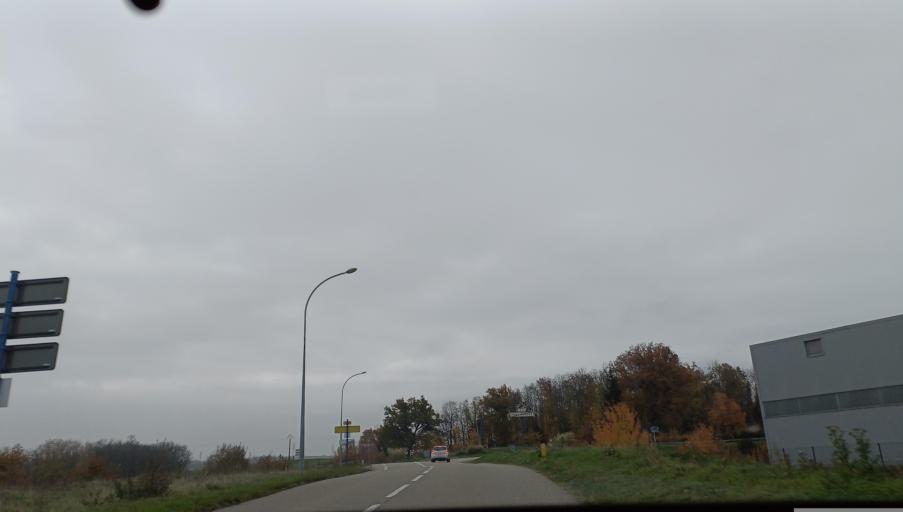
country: FR
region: Rhone-Alpes
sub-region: Departement de l'Isere
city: Pont-Eveque
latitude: 45.5272
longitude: 4.9277
